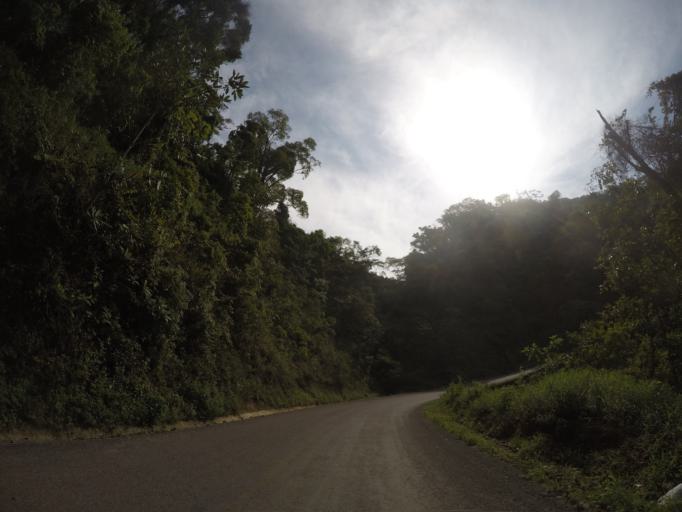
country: MX
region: Oaxaca
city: Pluma Hidalgo
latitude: 15.9337
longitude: -96.4243
